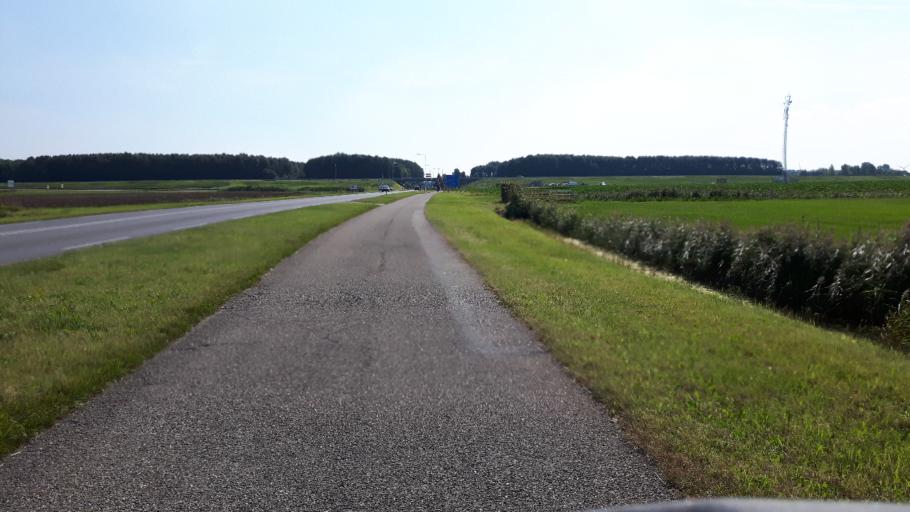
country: NL
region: Friesland
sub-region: Gemeente Franekeradeel
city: Franeker
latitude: 53.2046
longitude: 5.5420
